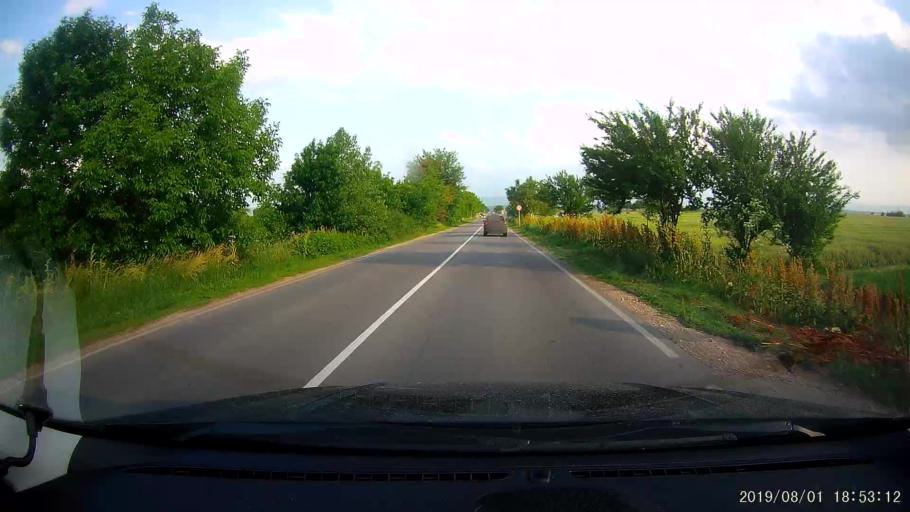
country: BG
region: Shumen
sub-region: Obshtina Shumen
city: Shumen
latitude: 43.2242
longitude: 26.9913
